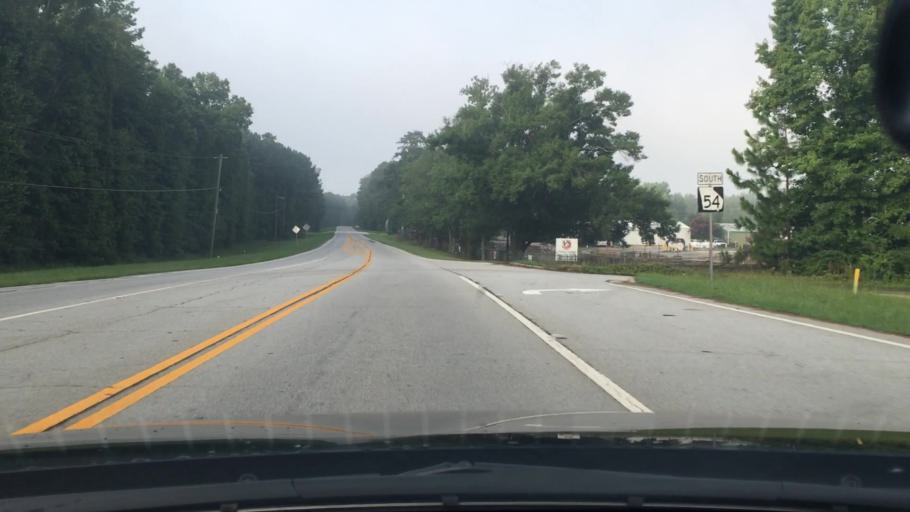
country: US
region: Georgia
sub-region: Fayette County
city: Peachtree City
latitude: 33.3600
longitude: -84.6344
